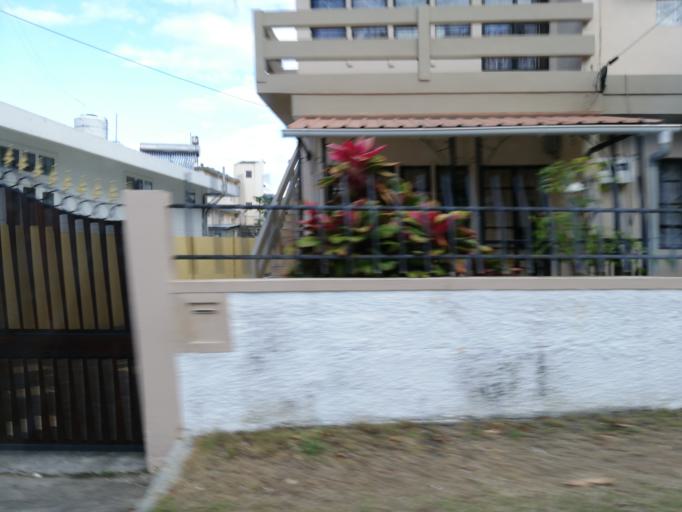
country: MU
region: Plaines Wilhems
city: Ebene
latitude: -20.2346
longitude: 57.4602
